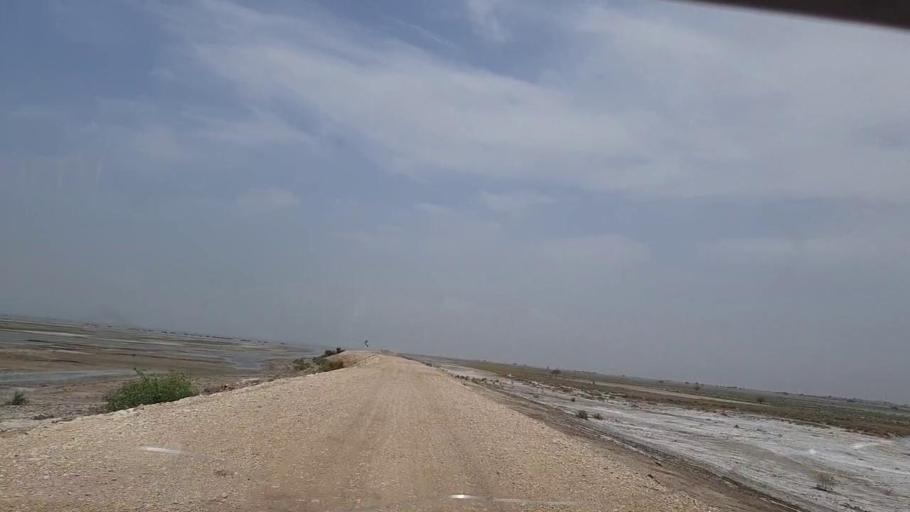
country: PK
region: Sindh
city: Sehwan
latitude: 26.4162
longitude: 67.7538
